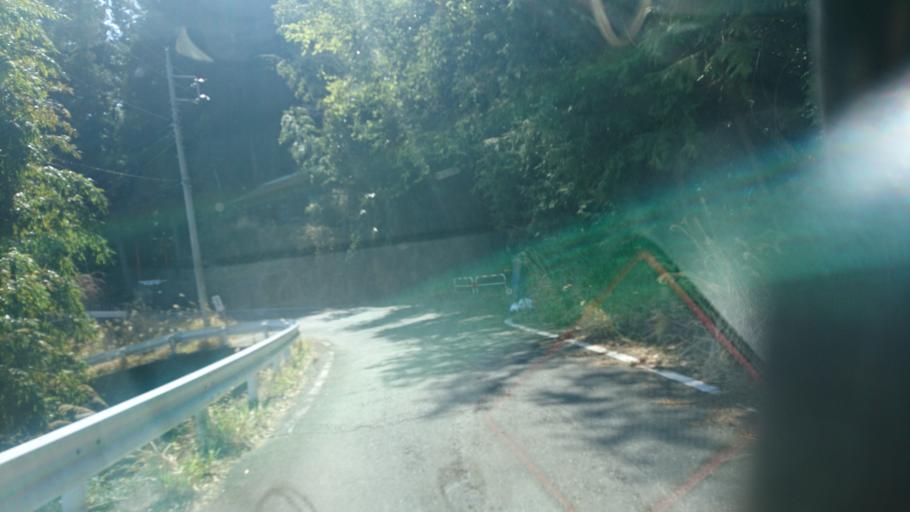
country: JP
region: Shizuoka
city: Fujinomiya
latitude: 35.3269
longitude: 138.4398
